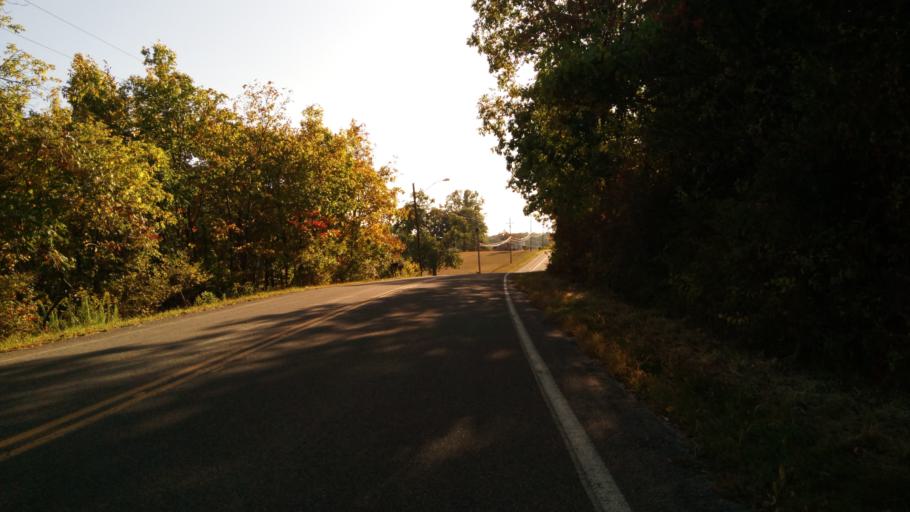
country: US
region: New York
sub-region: Chemung County
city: West Elmira
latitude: 42.0721
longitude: -76.8286
